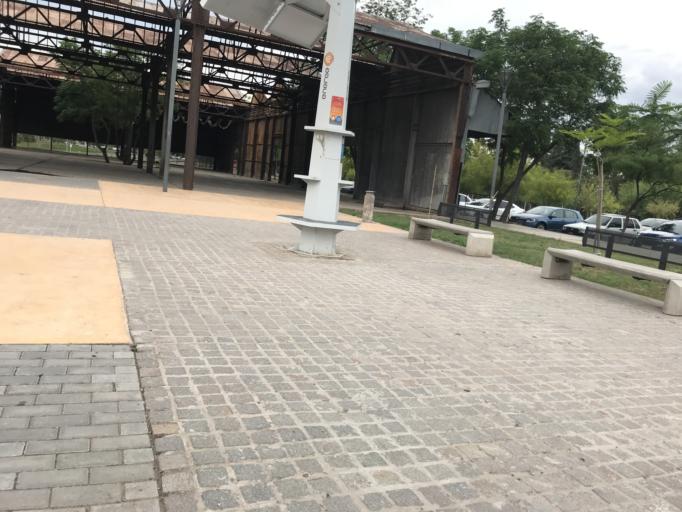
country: AR
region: Mendoza
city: Mendoza
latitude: -32.8771
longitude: -68.8401
